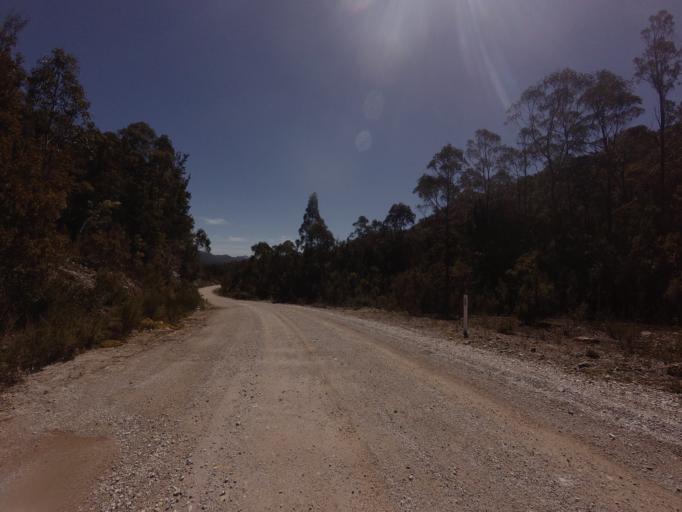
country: AU
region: Tasmania
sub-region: Huon Valley
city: Geeveston
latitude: -42.8179
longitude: 146.3871
